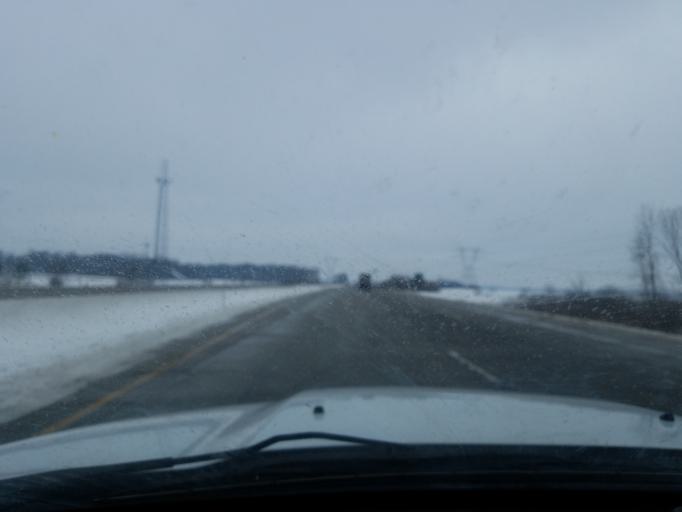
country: US
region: Indiana
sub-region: Marshall County
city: Argos
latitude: 41.2001
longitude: -86.2561
